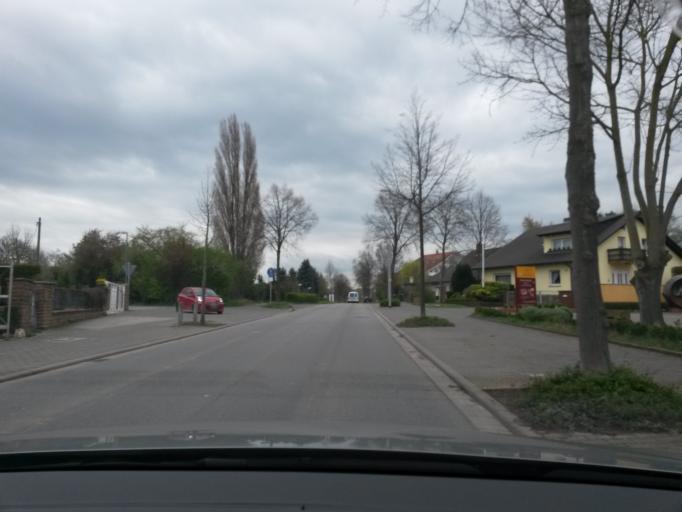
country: DE
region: Rheinland-Pfalz
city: Morstadt
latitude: 49.6764
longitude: 8.2896
